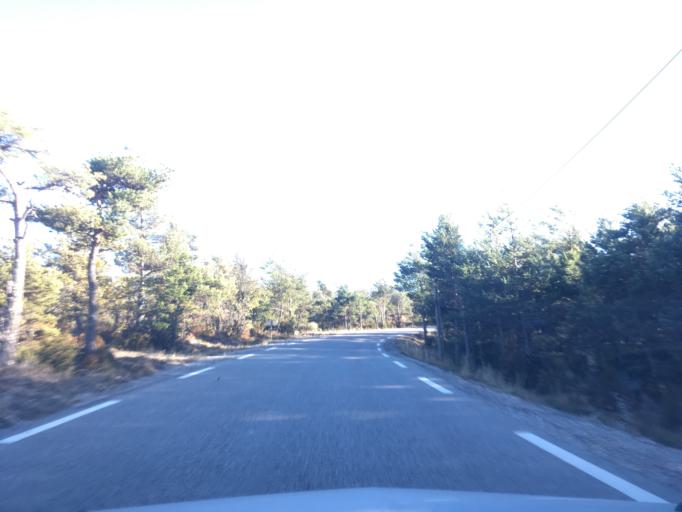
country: FR
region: Provence-Alpes-Cote d'Azur
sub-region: Departement des Alpes-de-Haute-Provence
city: Castellane
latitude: 43.7453
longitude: 6.4361
